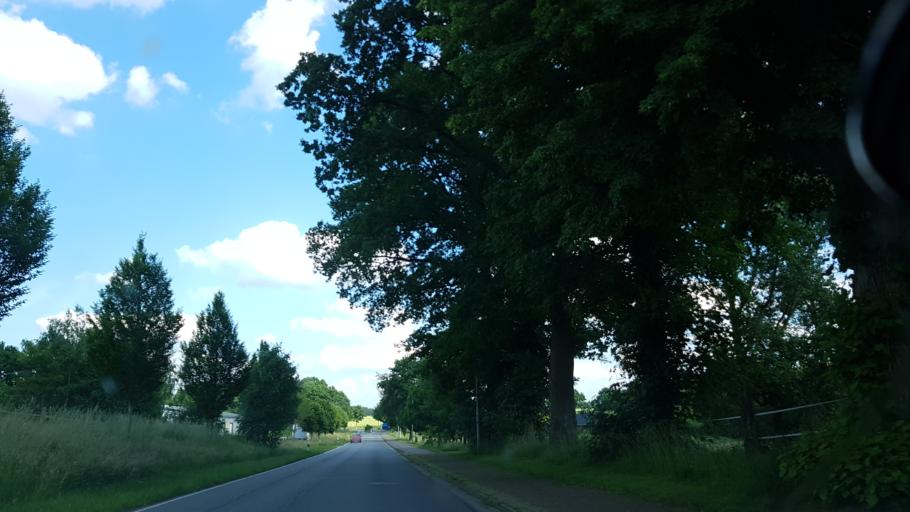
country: DE
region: Lower Saxony
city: Wenzendorf
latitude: 53.3489
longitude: 9.7797
